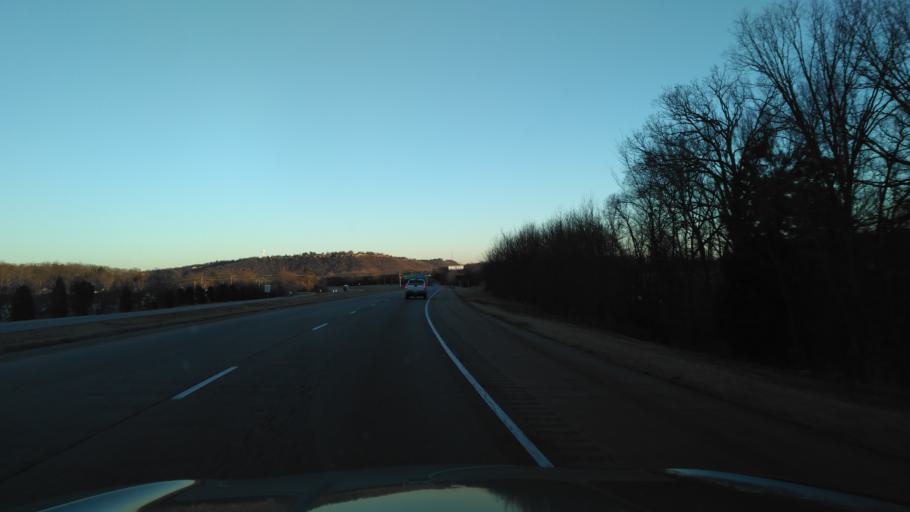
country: US
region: Arkansas
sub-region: Crawford County
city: Van Buren
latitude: 35.4622
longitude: -94.4059
